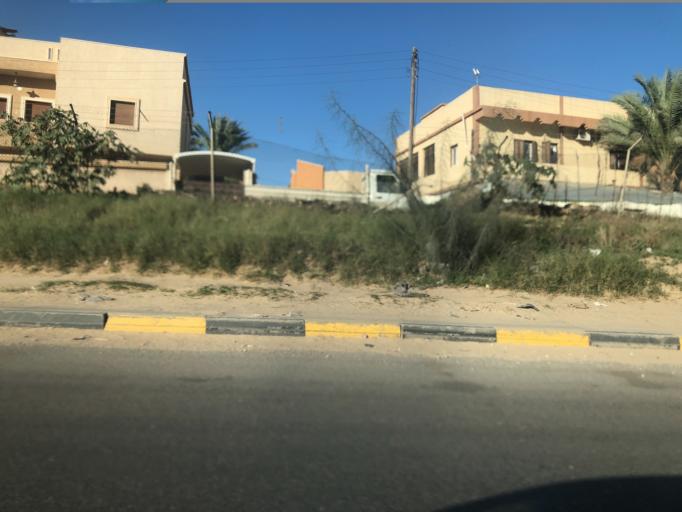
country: LY
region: Tripoli
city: Tagiura
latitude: 32.8699
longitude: 13.2708
